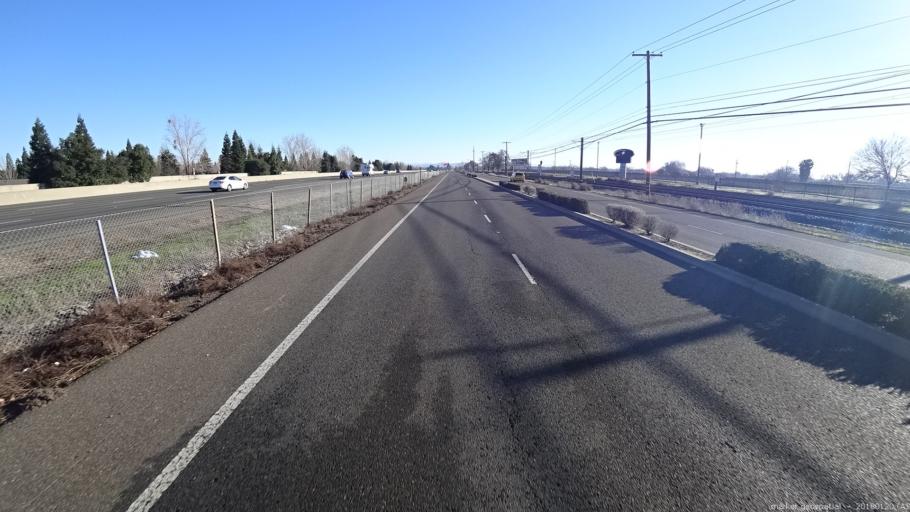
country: US
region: California
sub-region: Sacramento County
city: Gold River
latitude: 38.6214
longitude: -121.2366
